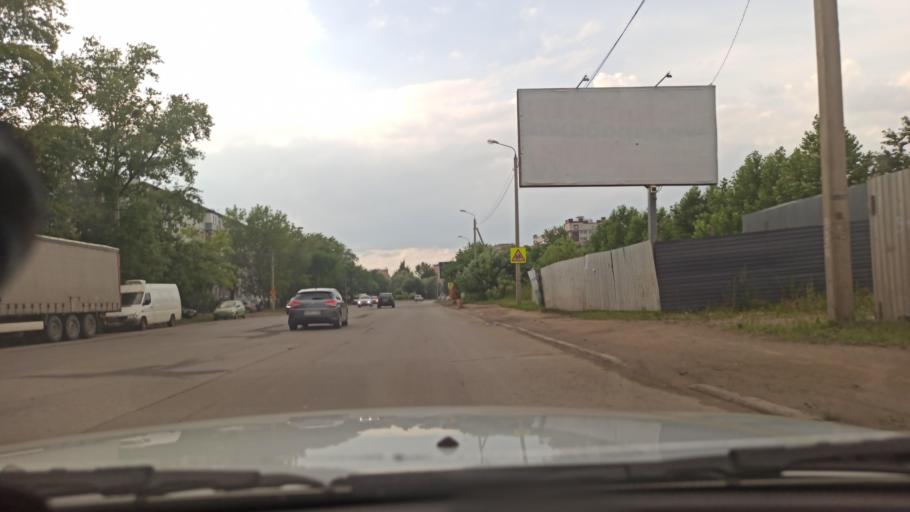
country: RU
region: Vologda
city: Vologda
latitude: 59.2047
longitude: 39.8513
